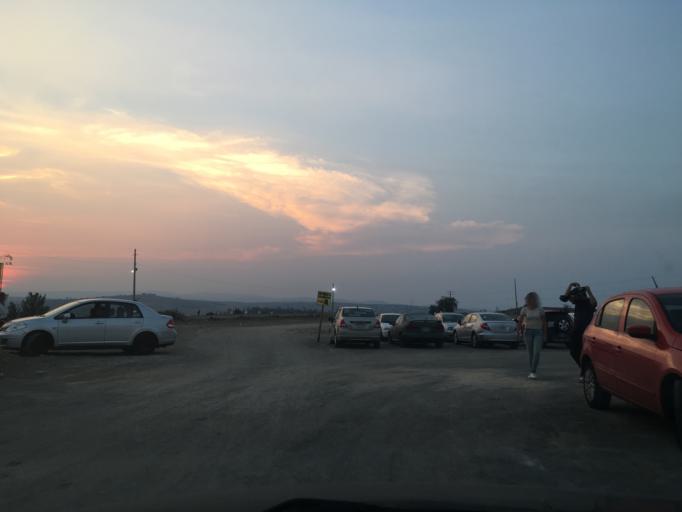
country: MX
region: Michoacan
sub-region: Morelia
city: La Aldea
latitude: 19.7305
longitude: -101.0916
